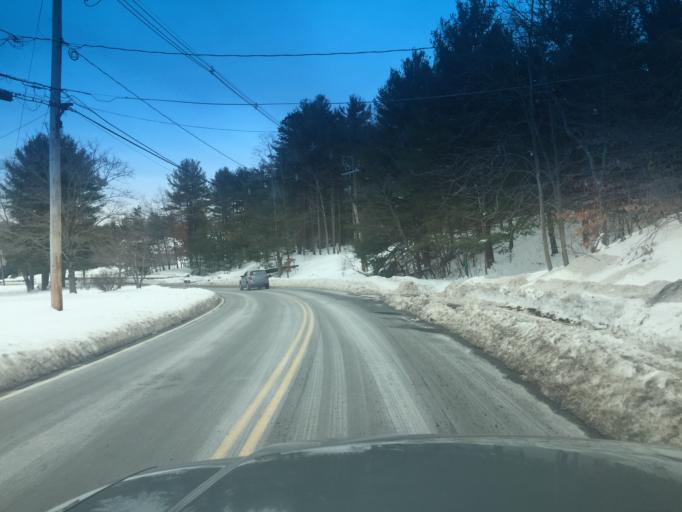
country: US
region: Massachusetts
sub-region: Norfolk County
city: Norfolk
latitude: 42.1039
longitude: -71.2820
